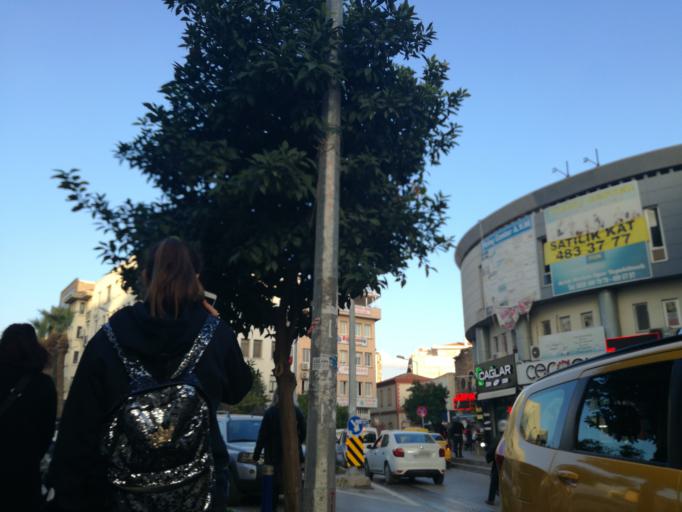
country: TR
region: Izmir
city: Izmir
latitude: 38.4214
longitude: 27.1313
